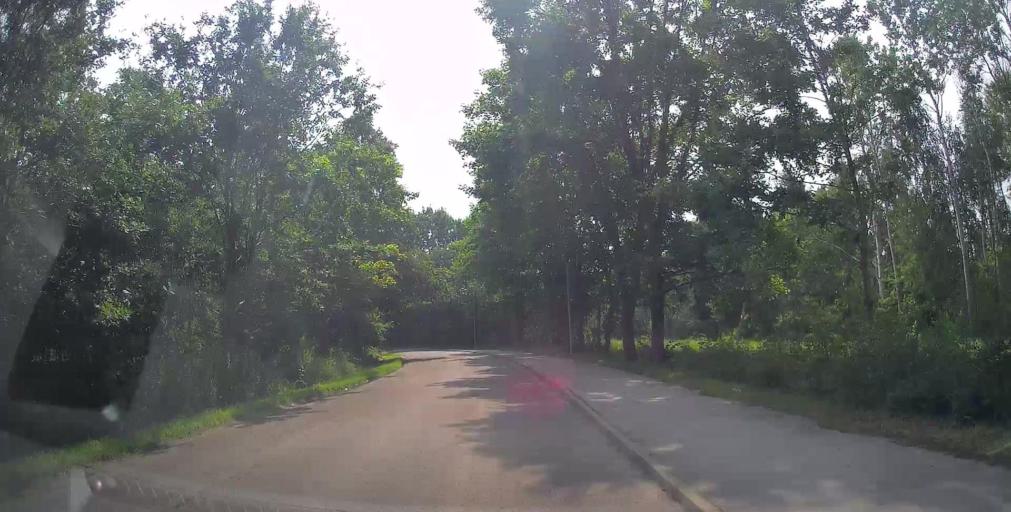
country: PL
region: Masovian Voivodeship
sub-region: Powiat bialobrzeski
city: Bialobrzegi
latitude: 51.6349
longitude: 20.9534
